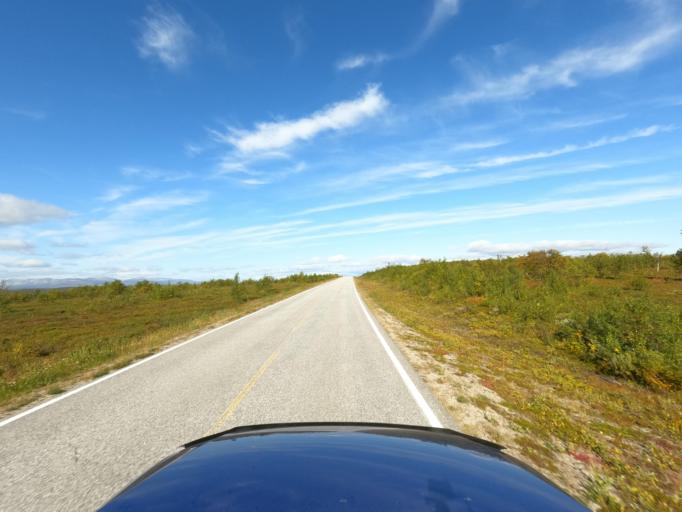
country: NO
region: Finnmark Fylke
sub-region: Karasjok
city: Karasjohka
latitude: 69.7116
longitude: 25.2415
